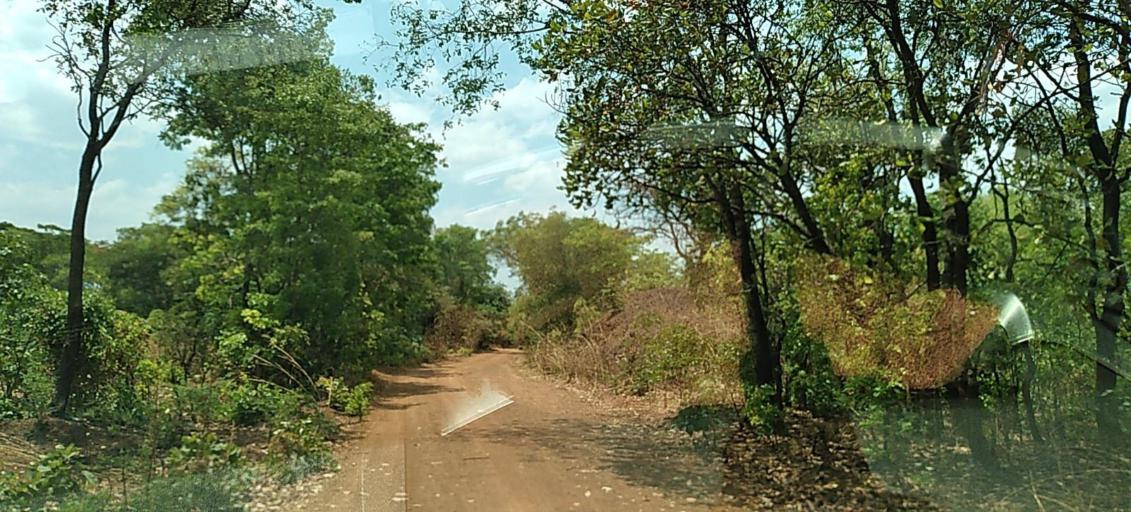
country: ZM
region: Copperbelt
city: Chingola
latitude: -12.5459
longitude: 27.6316
